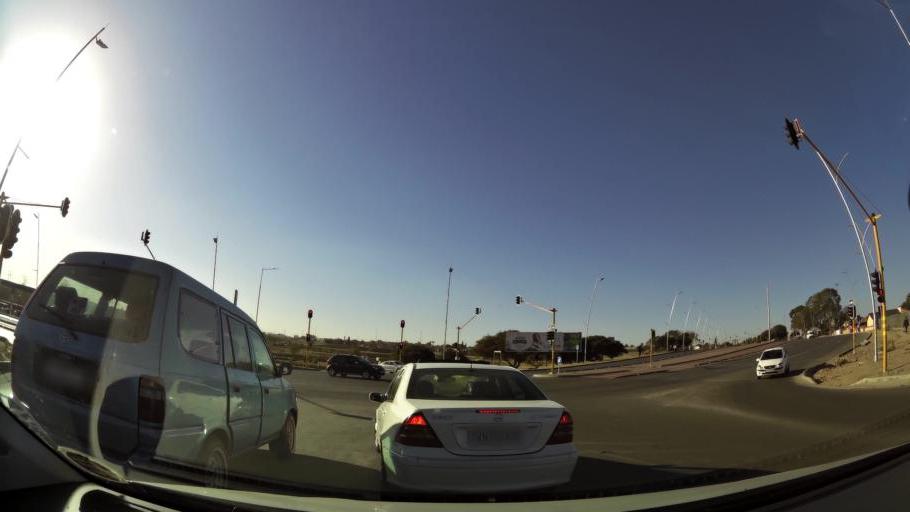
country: ZA
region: Gauteng
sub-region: Ekurhuleni Metropolitan Municipality
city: Tembisa
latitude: -26.0178
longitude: 28.2159
